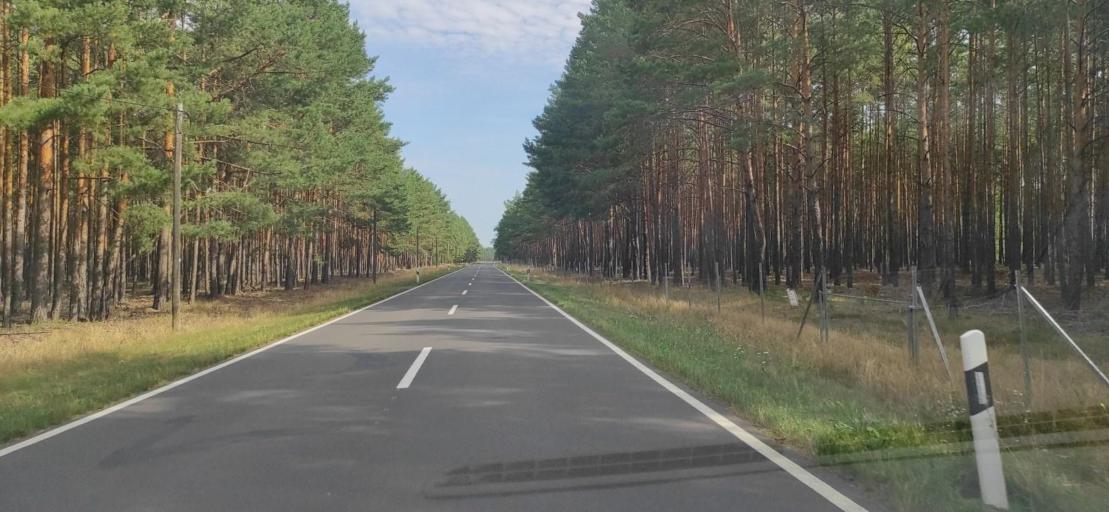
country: PL
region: Lubusz
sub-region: Powiat zarski
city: Trzebiel
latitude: 51.6352
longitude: 14.7446
